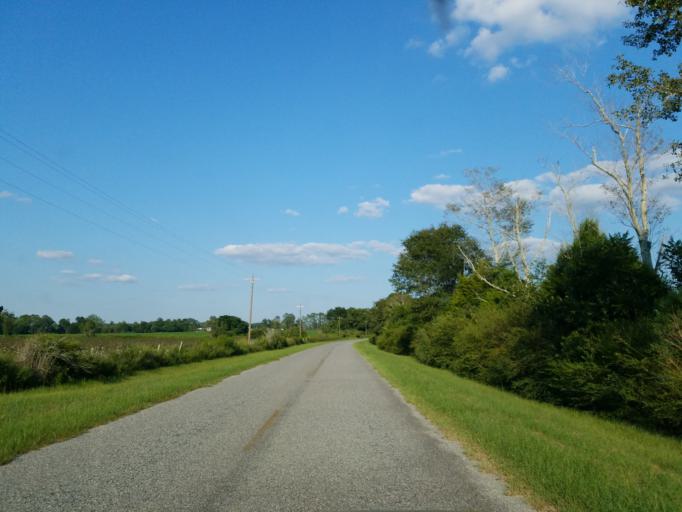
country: US
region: Georgia
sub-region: Cook County
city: Sparks
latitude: 31.2368
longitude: -83.4844
